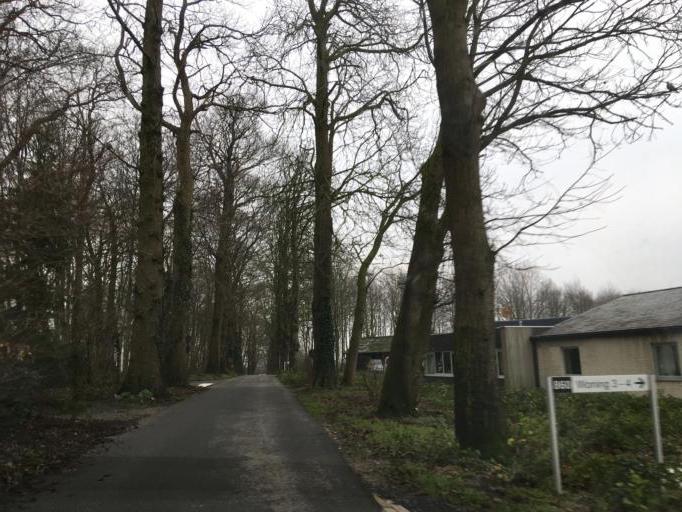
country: BE
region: Flanders
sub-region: Provincie West-Vlaanderen
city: Lichtervelde
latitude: 50.9978
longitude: 3.1250
